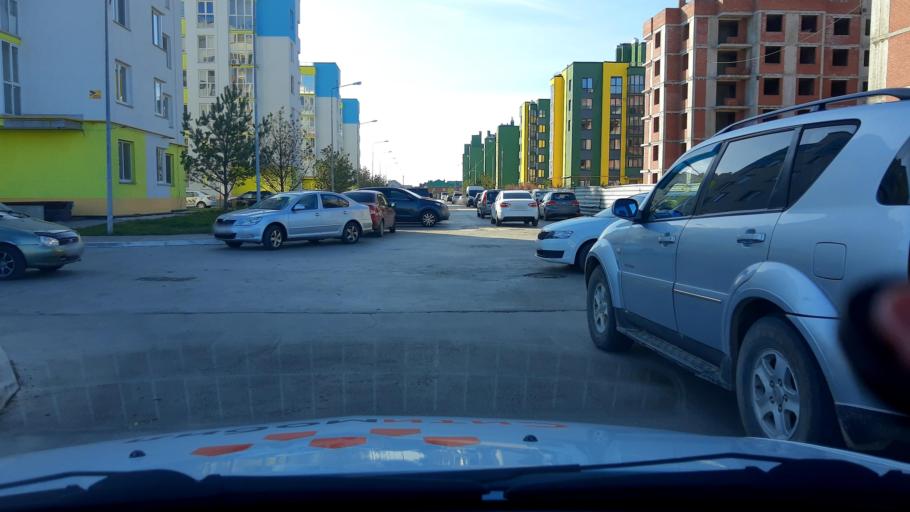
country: RU
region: Bashkortostan
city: Ufa
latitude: 54.7975
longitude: 55.9551
